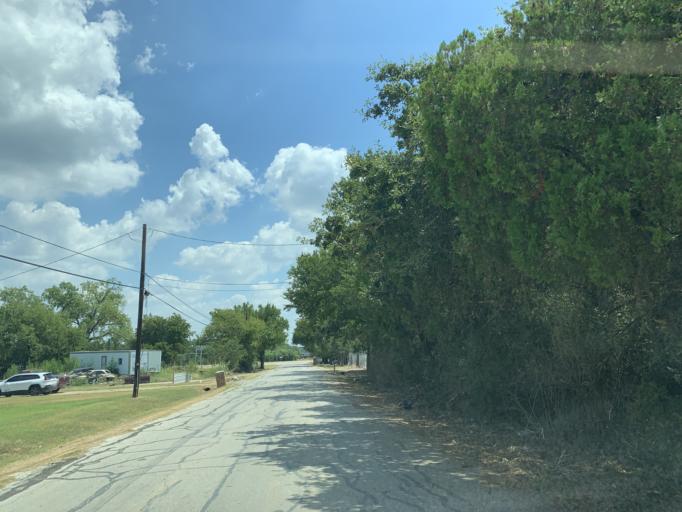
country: US
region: Texas
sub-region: Tarrant County
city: Lakeside
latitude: 32.8417
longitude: -97.4982
